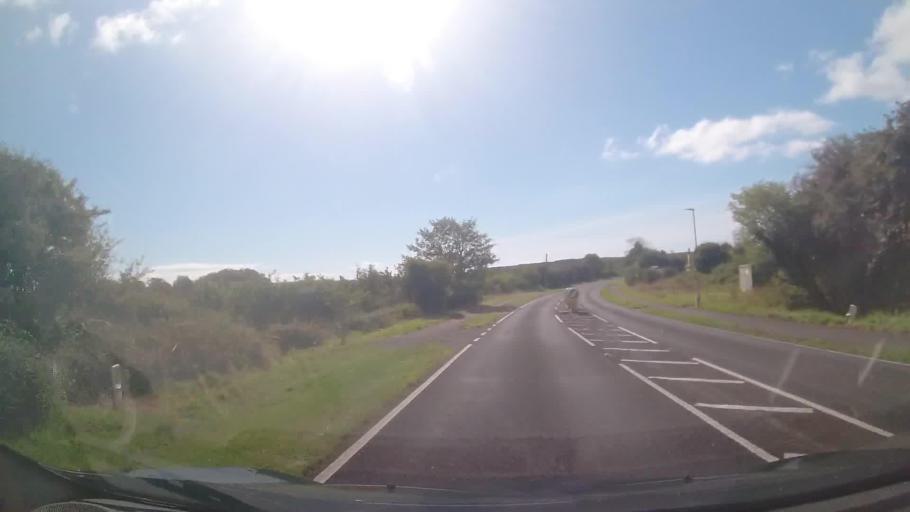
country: GB
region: Wales
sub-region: Pembrokeshire
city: Penally
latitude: 51.6639
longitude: -4.7201
